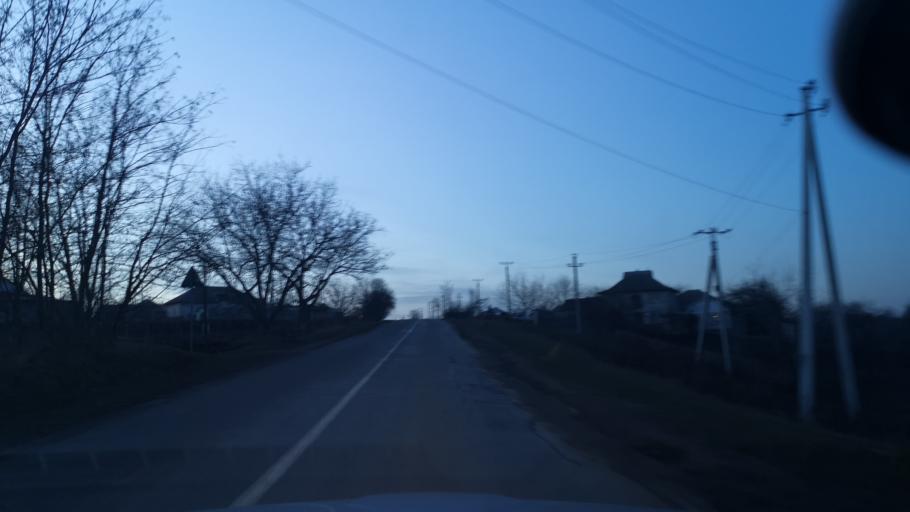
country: MD
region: Orhei
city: Orhei
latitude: 47.2860
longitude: 28.8728
